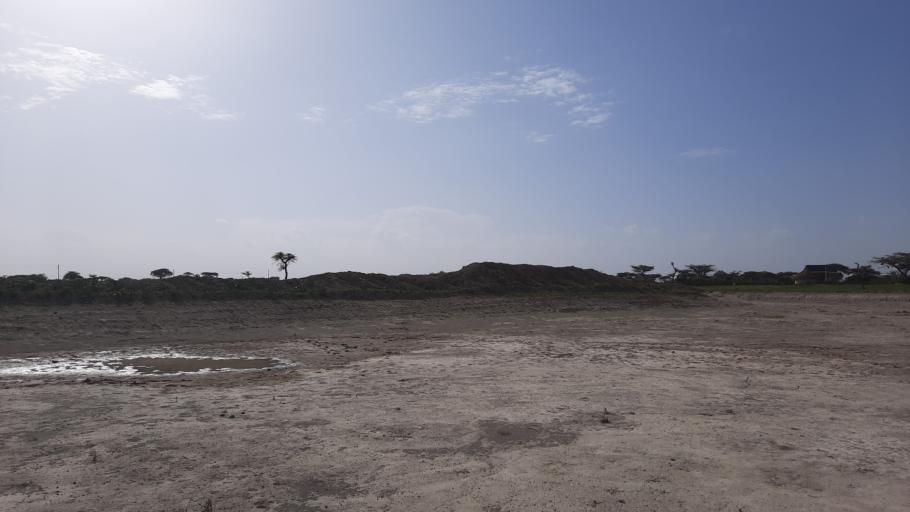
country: ET
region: Oromiya
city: Ziway
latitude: 7.6928
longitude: 38.6627
